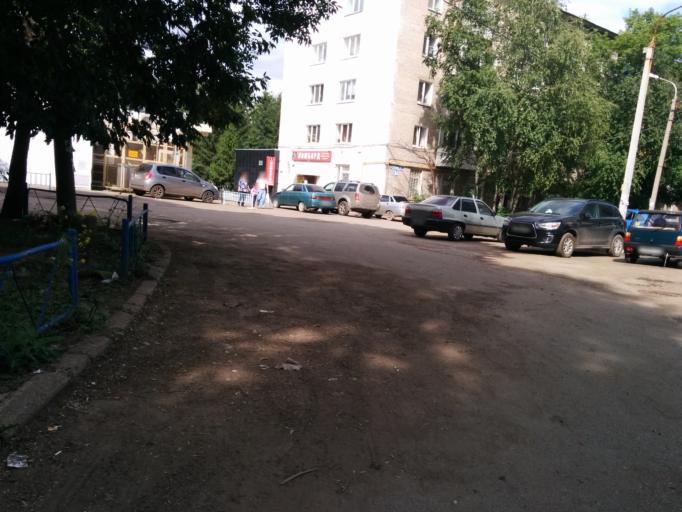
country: RU
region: Bashkortostan
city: Ufa
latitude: 54.7343
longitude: 55.9553
